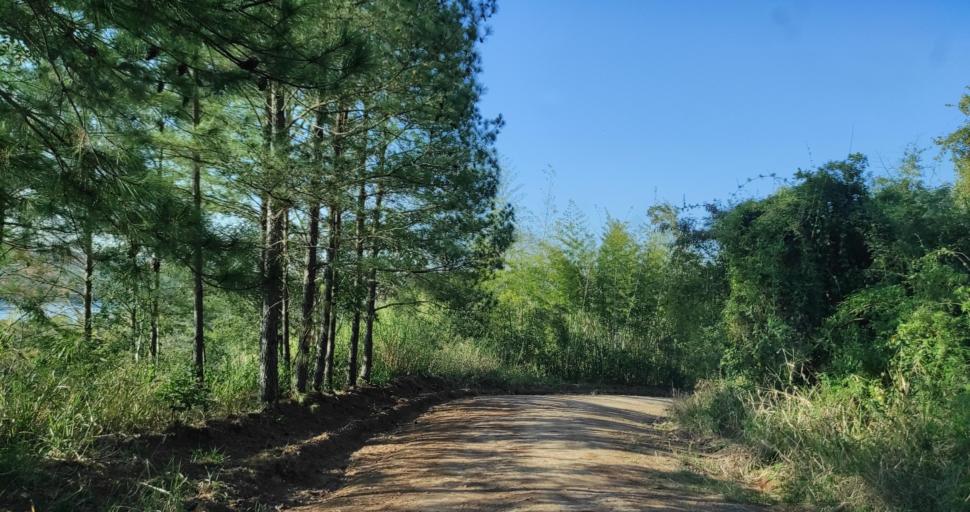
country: AR
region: Misiones
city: Capiovi
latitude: -26.8635
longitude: -55.1341
